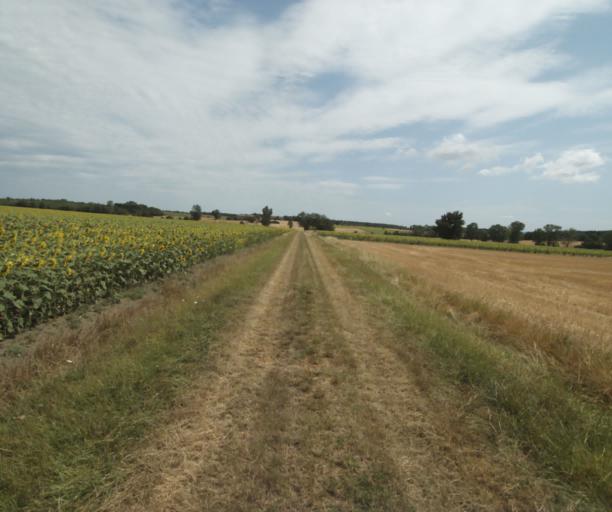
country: FR
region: Midi-Pyrenees
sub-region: Departement de la Haute-Garonne
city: Saint-Felix-Lauragais
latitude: 43.4142
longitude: 1.9170
